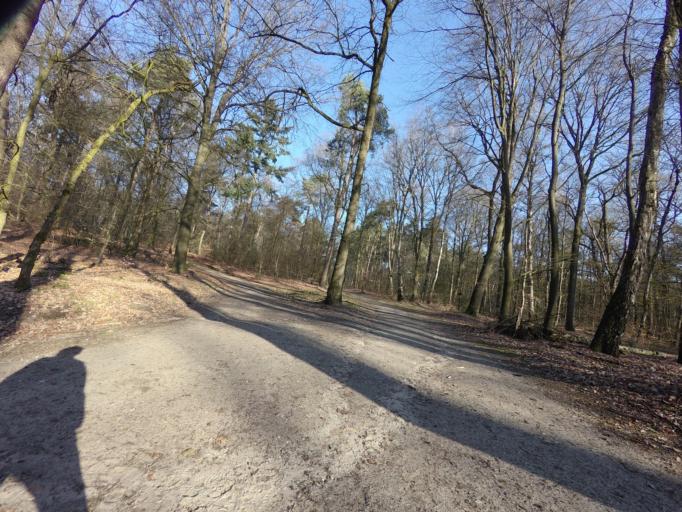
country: NL
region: Gelderland
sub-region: Gemeente Lochem
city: Barchem
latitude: 52.1407
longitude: 6.4307
